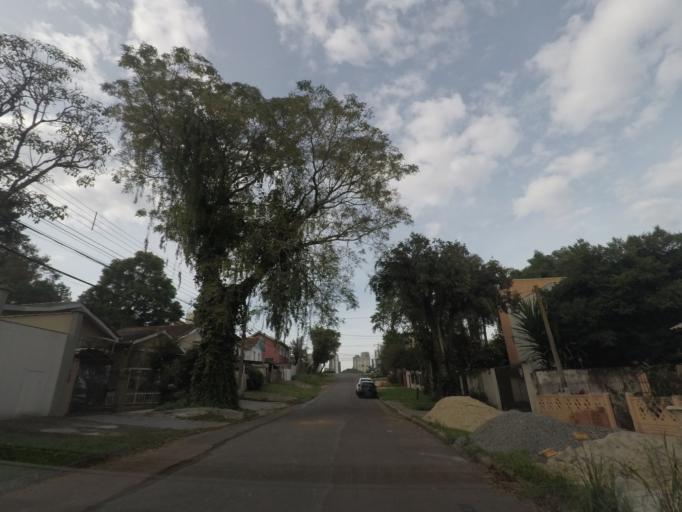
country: BR
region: Parana
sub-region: Curitiba
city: Curitiba
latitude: -25.4243
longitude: -49.2974
